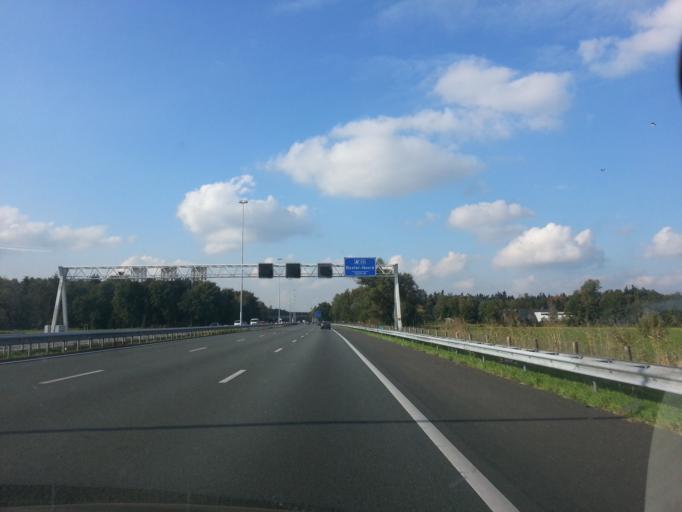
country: NL
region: North Brabant
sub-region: Gemeente Boxtel
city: Boxtel
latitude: 51.6050
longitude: 5.3307
